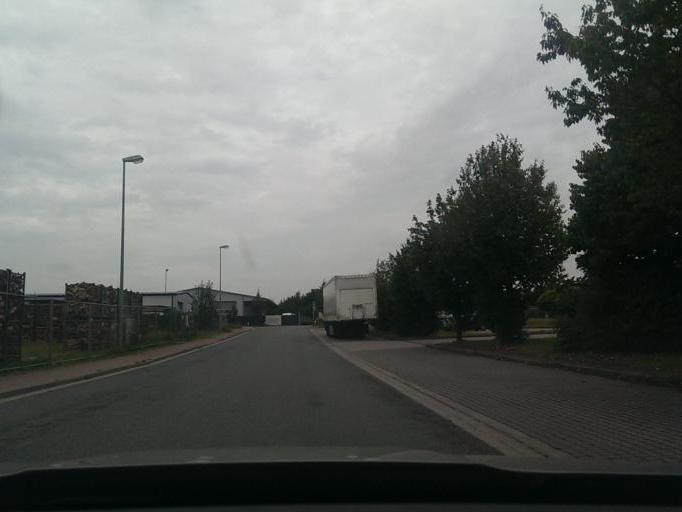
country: DE
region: Lower Saxony
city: Elze
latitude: 52.5168
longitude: 9.7358
